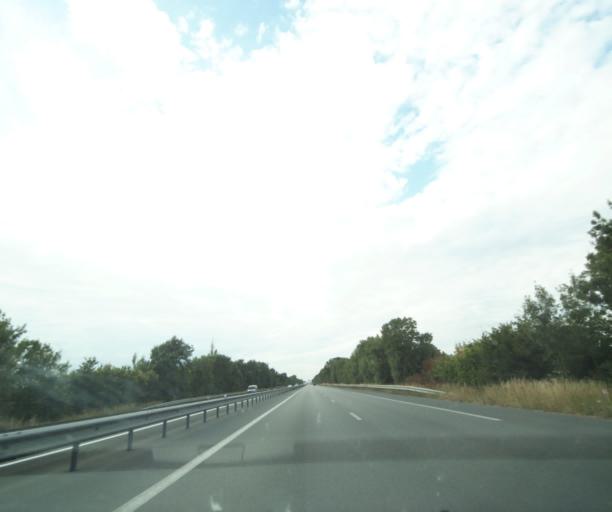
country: FR
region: Poitou-Charentes
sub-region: Departement de la Charente-Maritime
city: Chatelaillon-Plage
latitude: 46.0902
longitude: -1.0842
